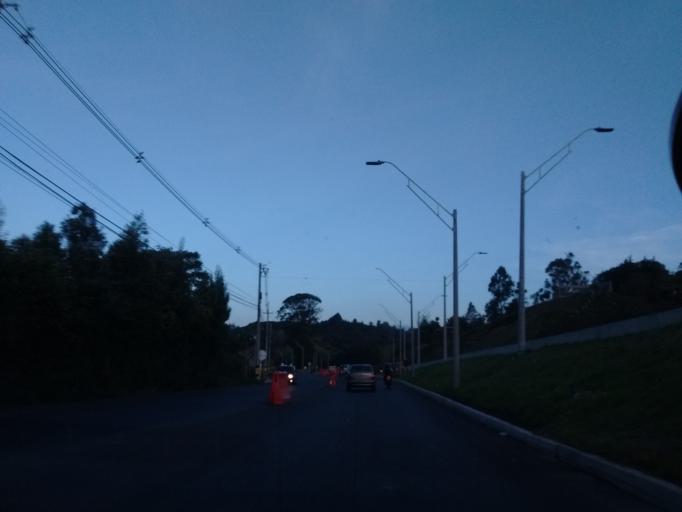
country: CO
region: Antioquia
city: Santuario
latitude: 6.1376
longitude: -75.2969
